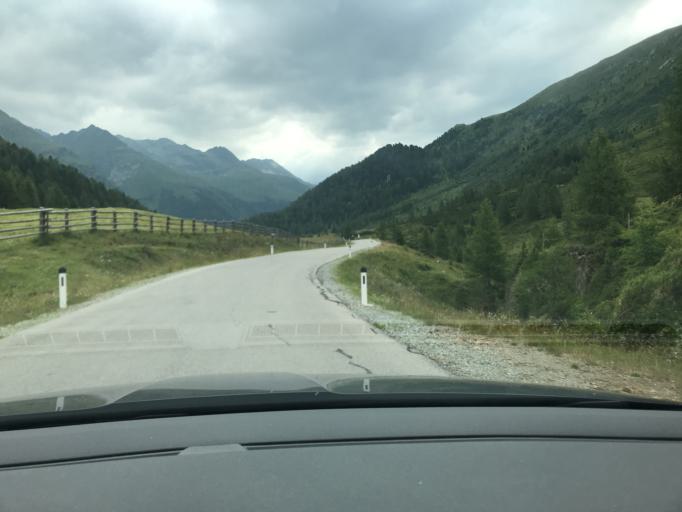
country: IT
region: Trentino-Alto Adige
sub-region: Bolzano
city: San Martino
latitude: 46.9015
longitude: 12.2245
